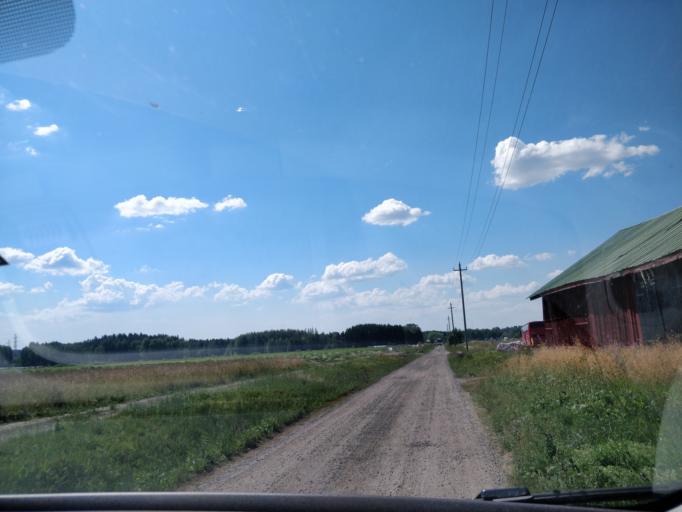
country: FI
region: Uusimaa
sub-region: Helsinki
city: Vantaa
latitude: 60.3081
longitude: 25.0792
